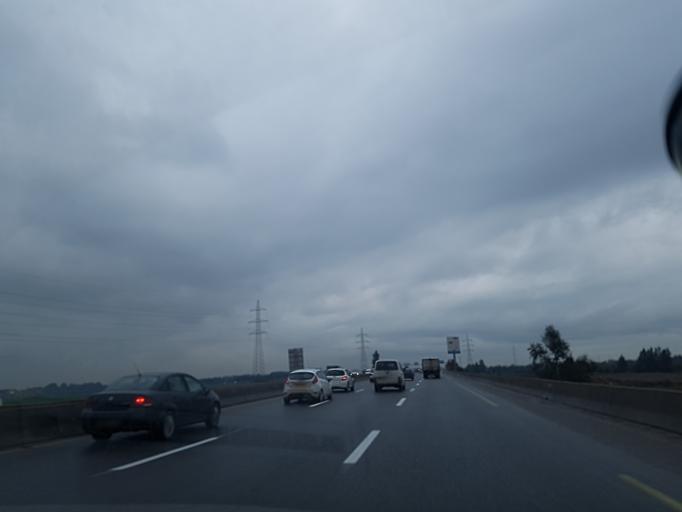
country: DZ
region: Boumerdes
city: Khemis el Khechna
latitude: 36.6690
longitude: 3.3166
